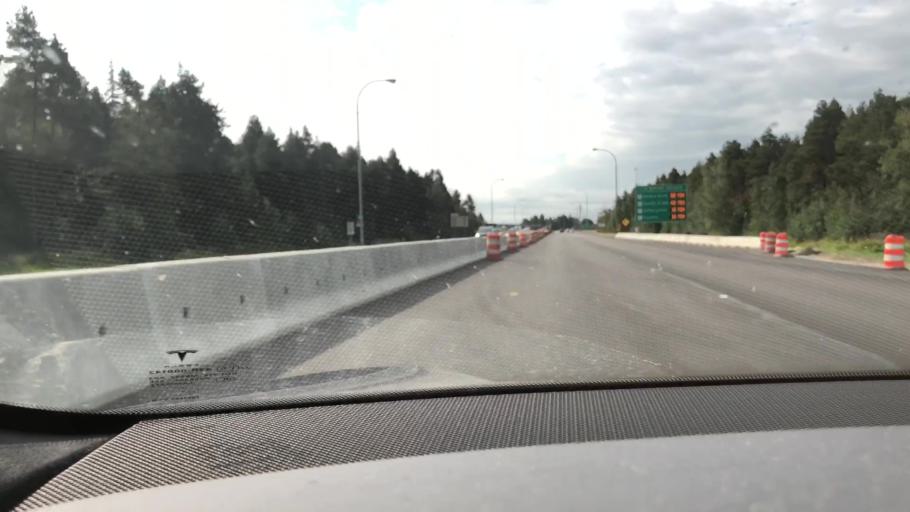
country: CA
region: British Columbia
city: Delta
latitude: 49.1276
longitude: -122.9282
